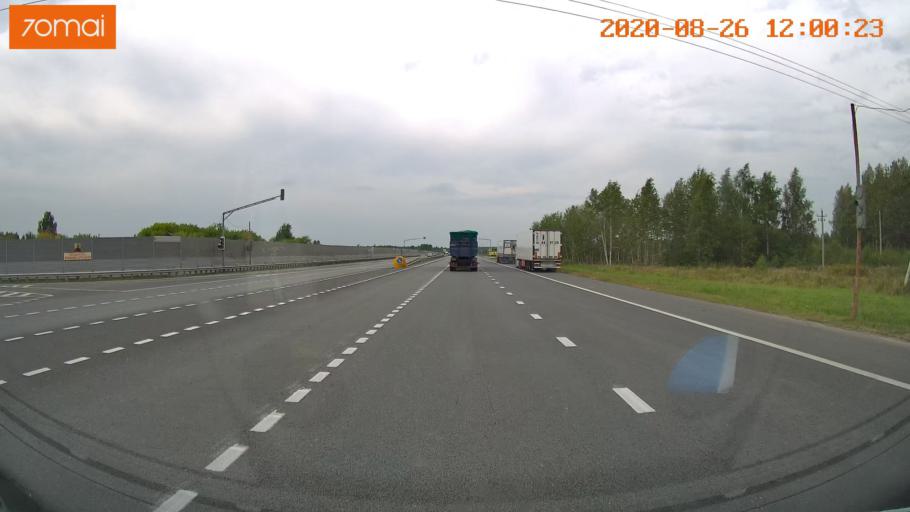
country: RU
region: Rjazan
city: Kiritsy
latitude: 54.2873
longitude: 40.2755
